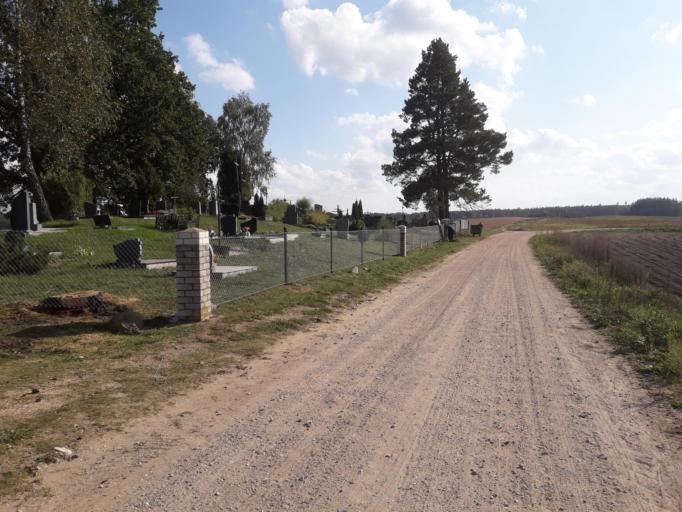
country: LT
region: Alytaus apskritis
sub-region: Alytaus rajonas
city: Daugai
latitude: 54.2358
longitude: 24.2247
